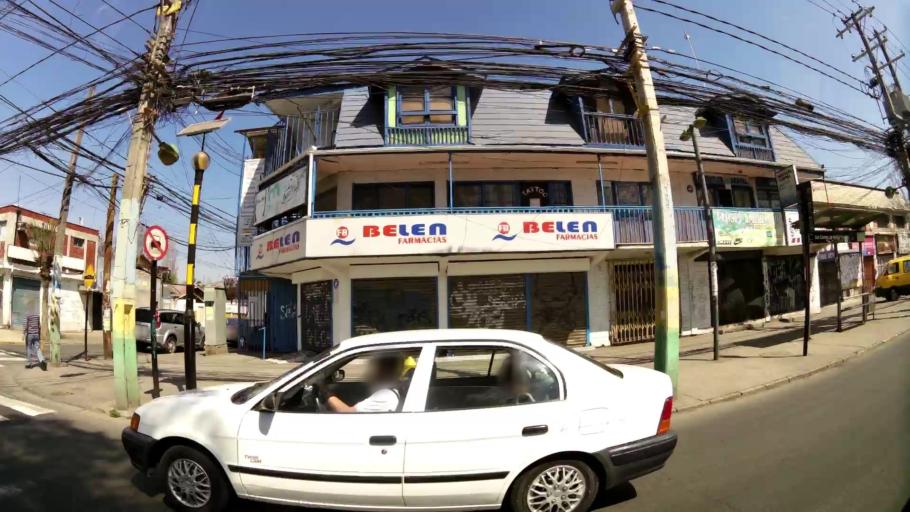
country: CL
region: Santiago Metropolitan
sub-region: Provincia de Santiago
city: Lo Prado
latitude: -33.3672
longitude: -70.7343
